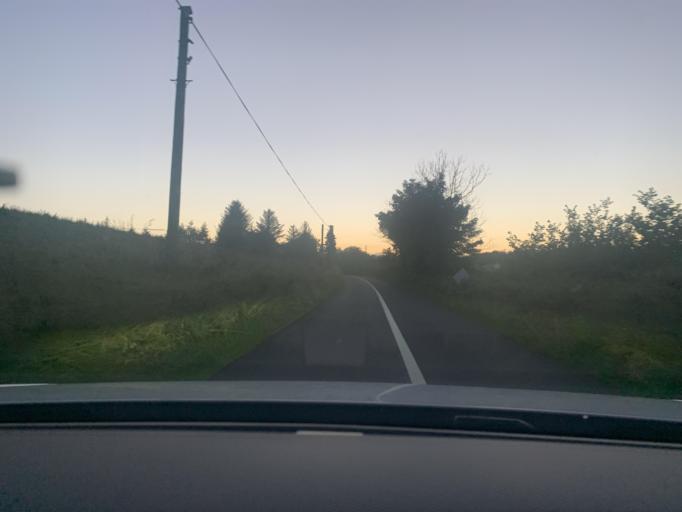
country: IE
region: Connaught
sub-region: County Leitrim
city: Manorhamilton
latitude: 54.2745
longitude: -8.3139
